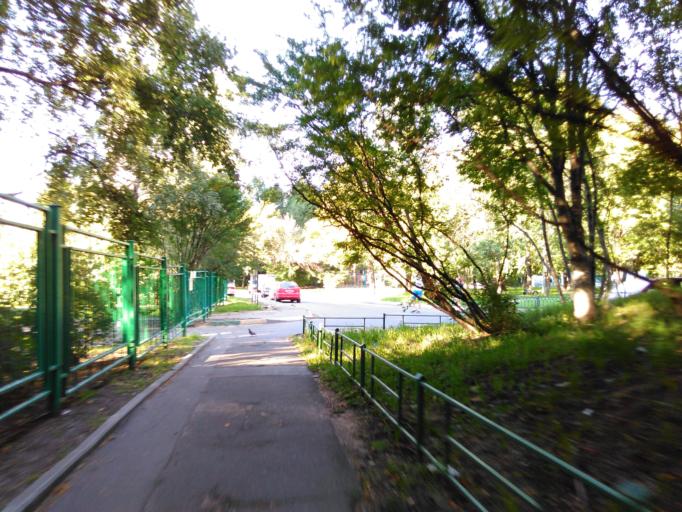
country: RU
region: Moscow
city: Tyoply Stan
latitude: 55.6268
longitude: 37.5052
